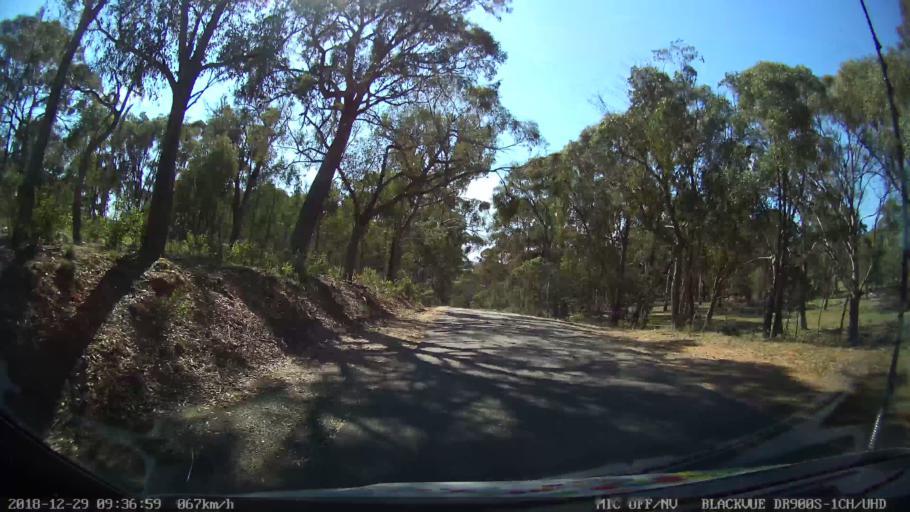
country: AU
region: New South Wales
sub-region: Upper Lachlan Shire
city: Crookwell
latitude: -34.6370
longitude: 149.3693
